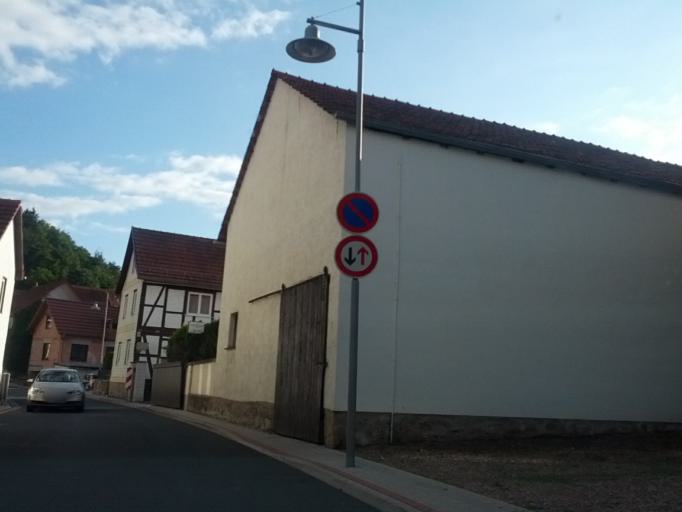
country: DE
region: Thuringia
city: Wolfsburg-Unkeroda
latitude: 50.9363
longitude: 10.2684
